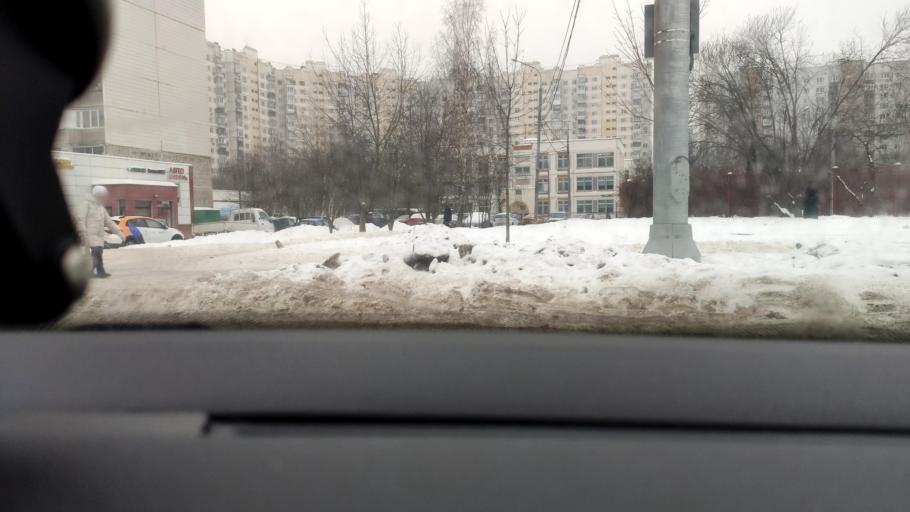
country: RU
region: Moskovskaya
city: Pavshino
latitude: 55.8543
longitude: 37.3470
